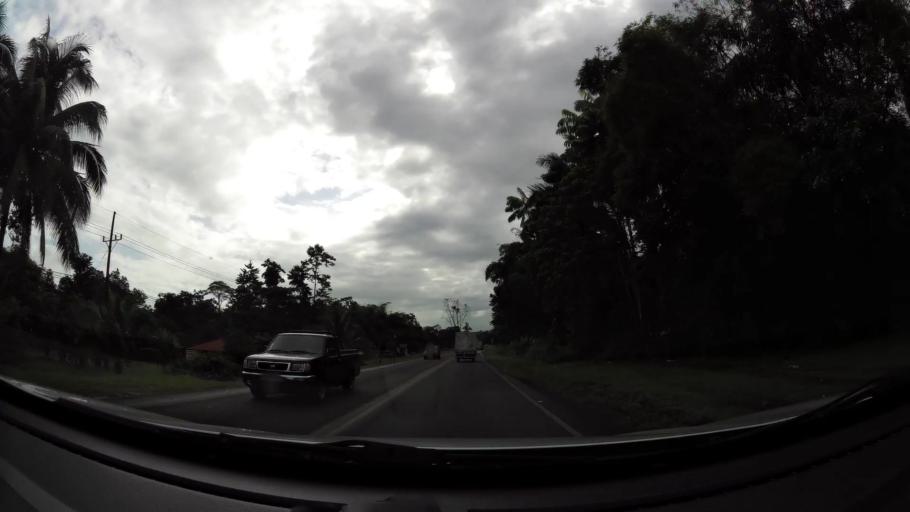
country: CR
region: Limon
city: Pocora
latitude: 10.1728
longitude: -83.6108
